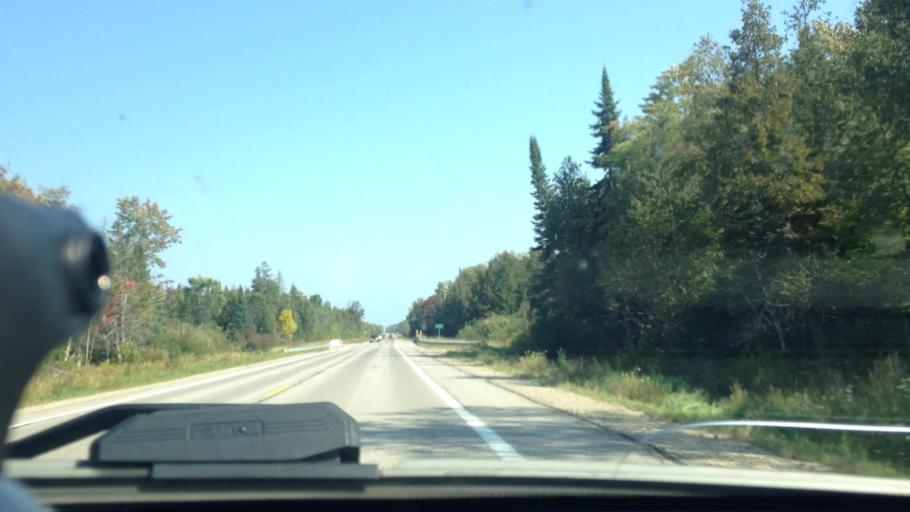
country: US
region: Michigan
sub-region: Luce County
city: Newberry
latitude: 46.3035
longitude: -85.3956
